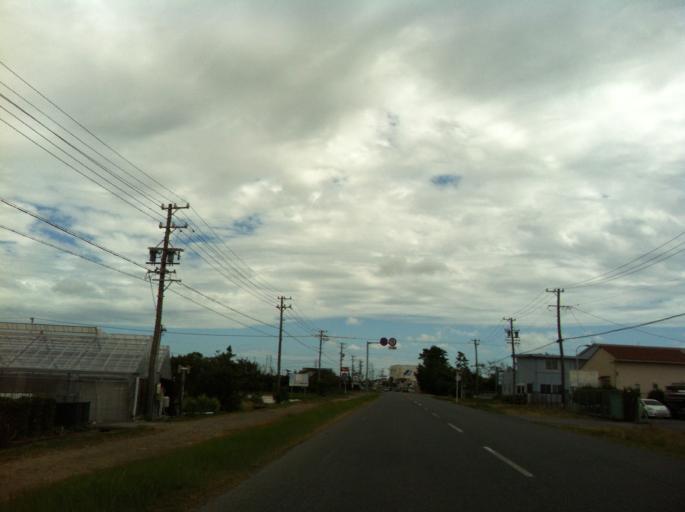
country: JP
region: Shizuoka
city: Kakegawa
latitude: 34.6562
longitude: 138.0554
